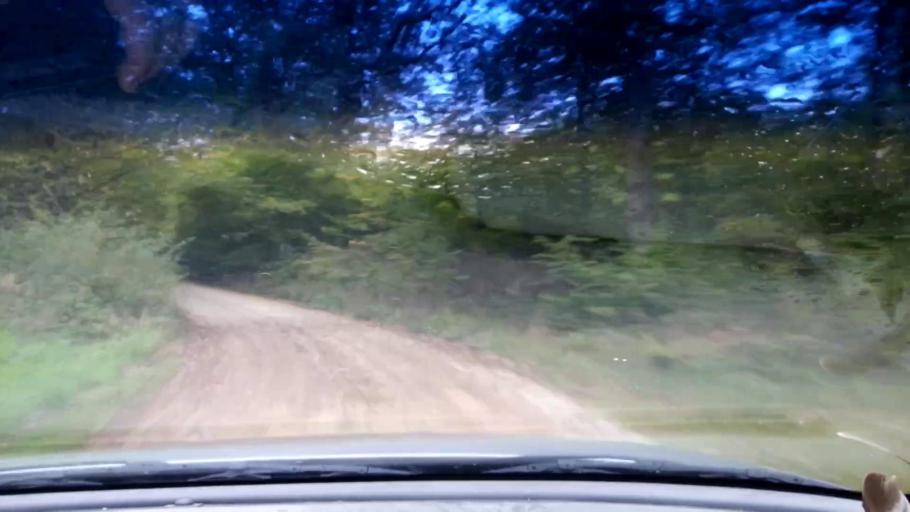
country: DE
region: Bavaria
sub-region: Upper Franconia
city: Burgwindheim
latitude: 49.8340
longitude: 10.6445
